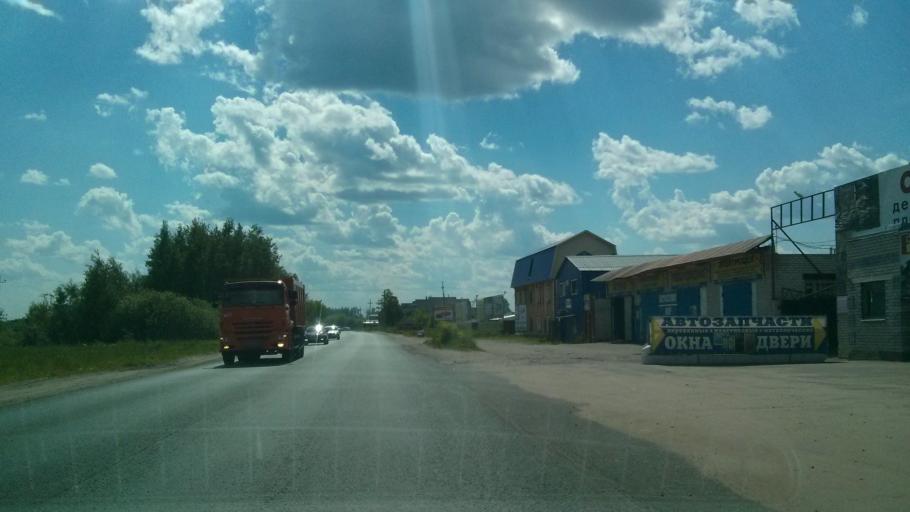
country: RU
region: Vladimir
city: Murom
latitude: 55.5560
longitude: 42.0097
